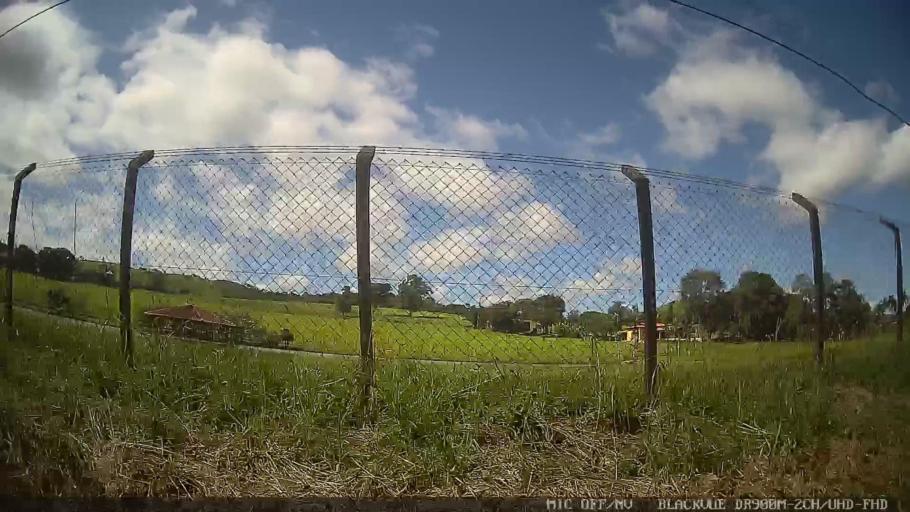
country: BR
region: Sao Paulo
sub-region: Amparo
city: Amparo
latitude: -22.8562
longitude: -46.7733
